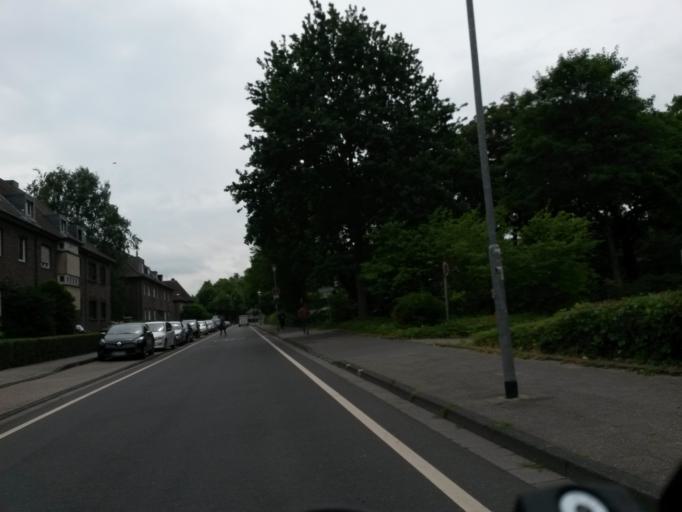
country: DE
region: North Rhine-Westphalia
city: Kempen
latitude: 51.3666
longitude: 6.4136
